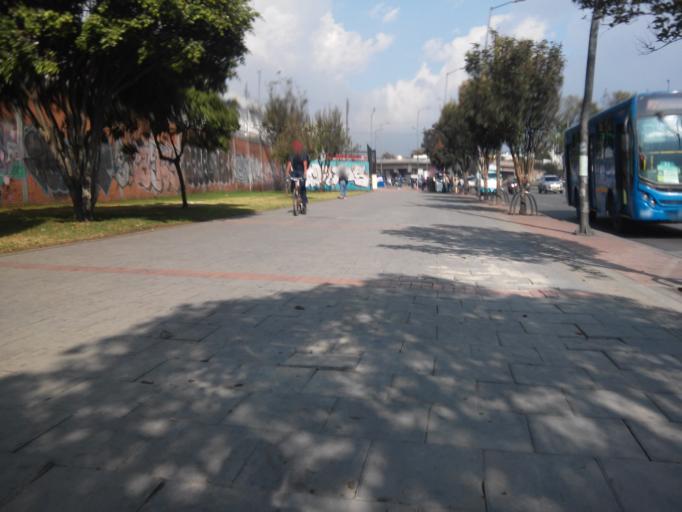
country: CO
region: Bogota D.C.
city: Bogota
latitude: 4.5953
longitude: -74.1473
